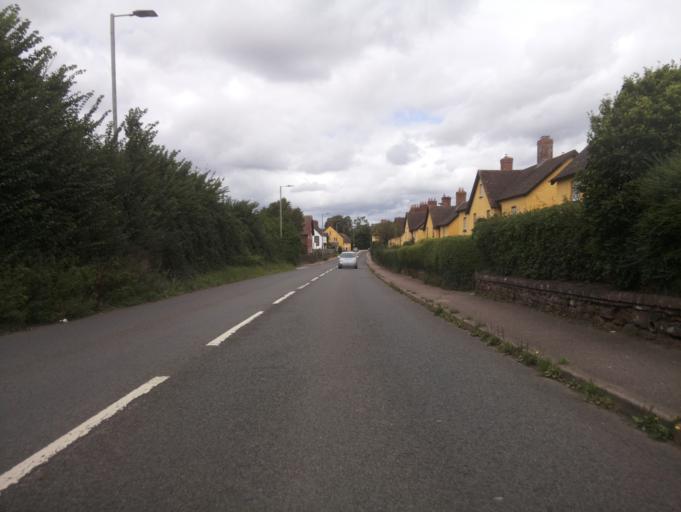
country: GB
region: England
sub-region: Devon
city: Heavitree
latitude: 50.7636
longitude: -3.4437
